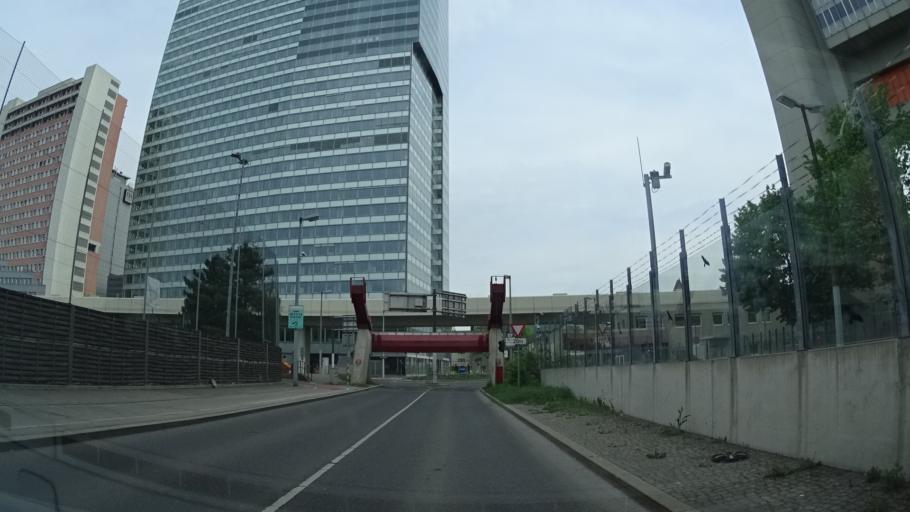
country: AT
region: Vienna
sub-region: Wien Stadt
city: Vienna
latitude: 48.2352
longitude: 16.4188
